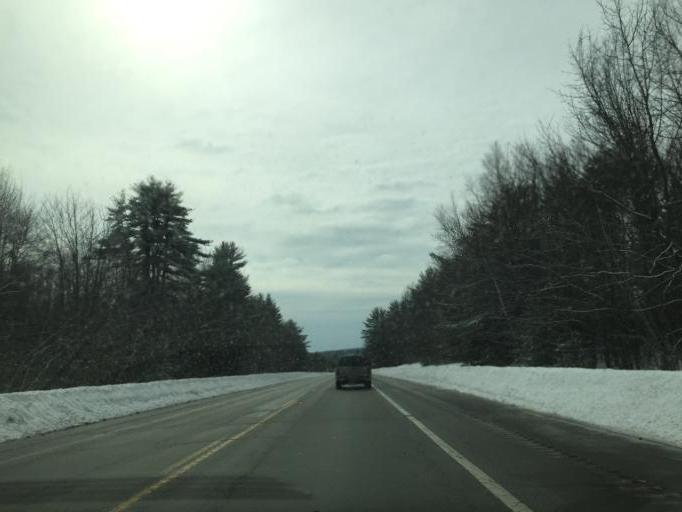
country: US
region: New Hampshire
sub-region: Strafford County
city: Rochester
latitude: 43.3572
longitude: -70.9865
